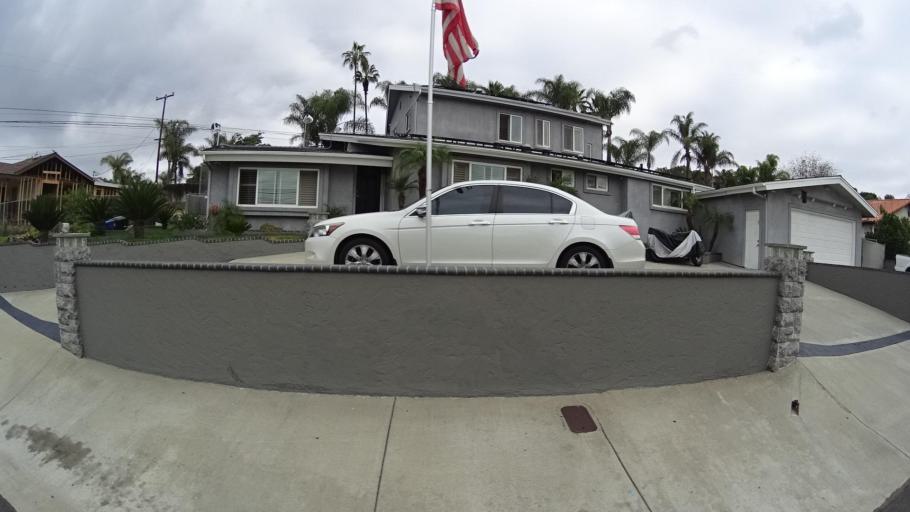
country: US
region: California
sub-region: San Diego County
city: Spring Valley
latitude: 32.7579
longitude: -116.9986
